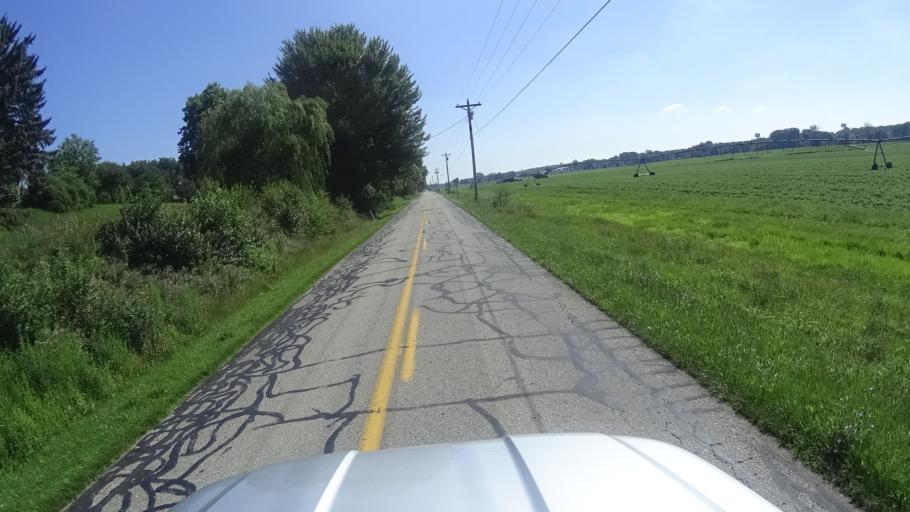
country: US
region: Indiana
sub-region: Madison County
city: Ingalls
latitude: 39.9807
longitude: -85.7859
